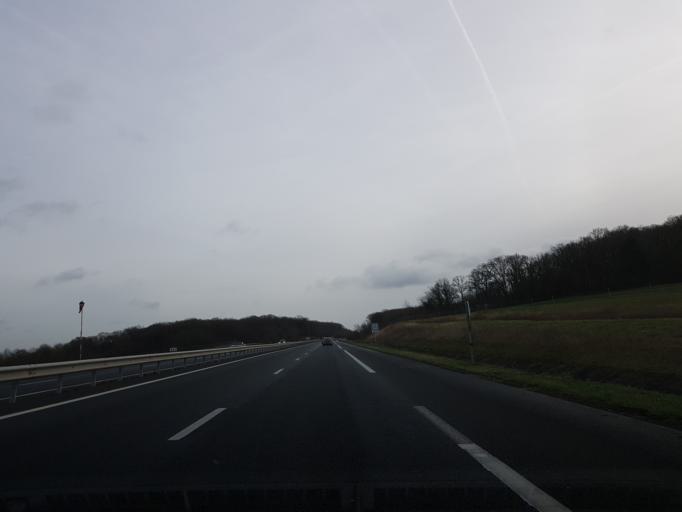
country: FR
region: Bourgogne
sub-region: Departement de l'Yonne
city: Soucy
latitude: 48.2443
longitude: 3.3569
